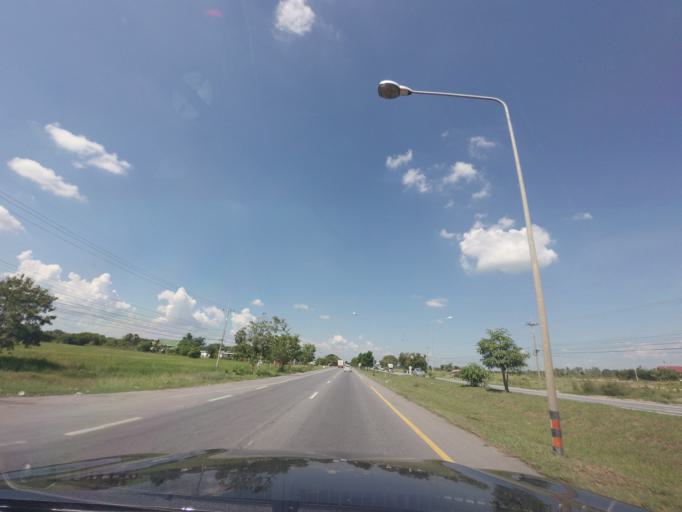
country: TH
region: Nakhon Ratchasima
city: Non Sung
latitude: 15.1276
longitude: 102.3053
